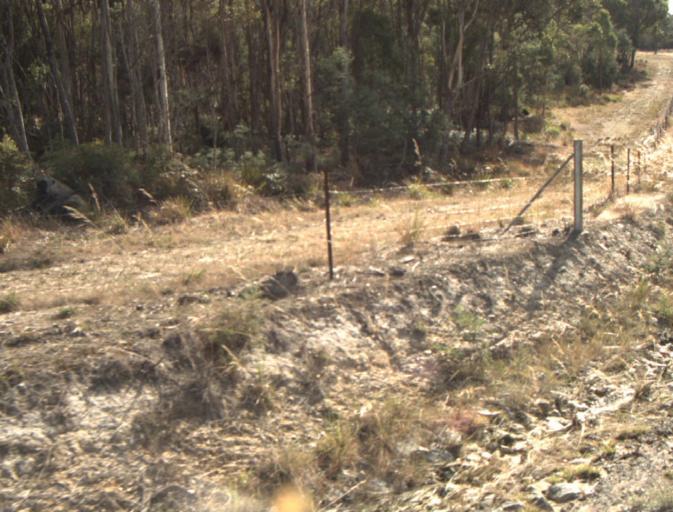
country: AU
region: Tasmania
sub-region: Launceston
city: Mayfield
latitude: -41.2110
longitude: 147.1334
